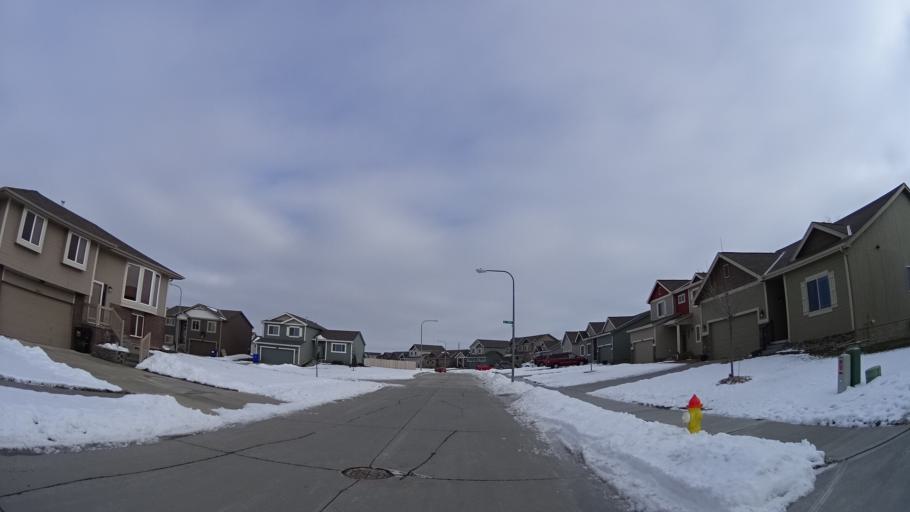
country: US
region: Nebraska
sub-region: Sarpy County
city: Offutt Air Force Base
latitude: 41.1040
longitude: -95.9804
